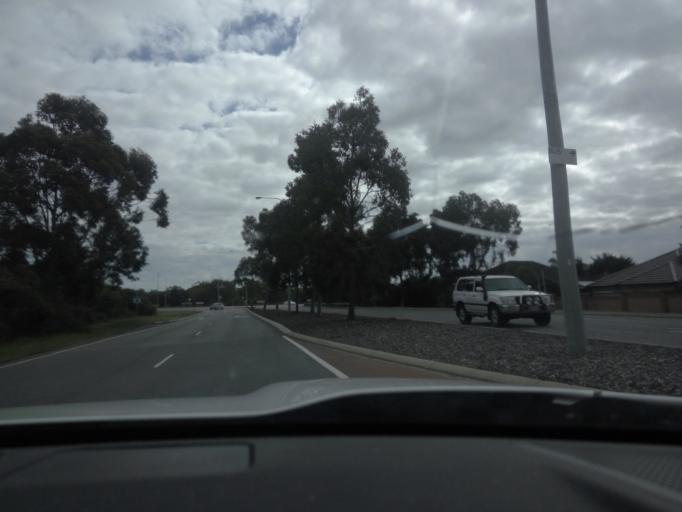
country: AU
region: Western Australia
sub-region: City of Cockburn
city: Bibra Lake
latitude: -32.1036
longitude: 115.8248
